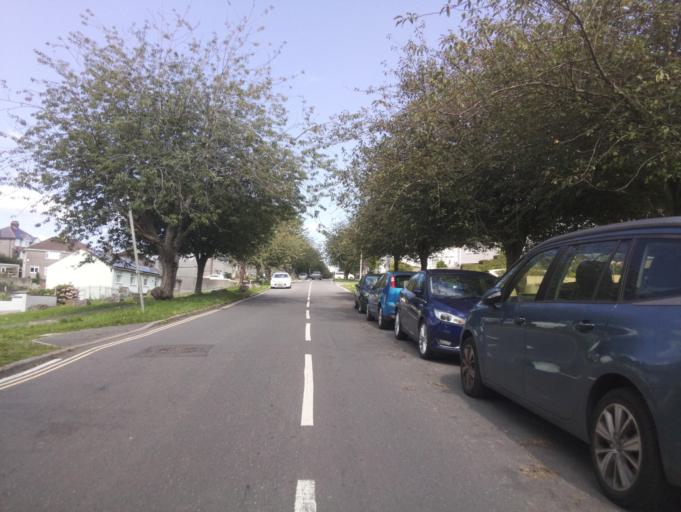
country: GB
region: England
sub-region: Plymouth
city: Plymouth
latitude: 50.3878
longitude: -4.1578
